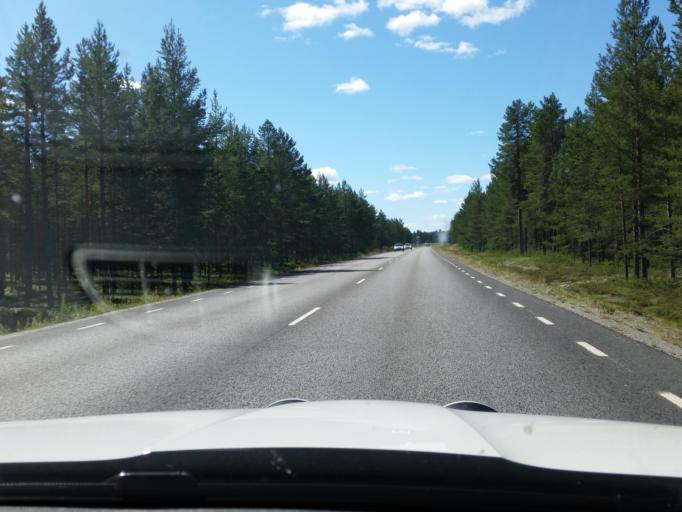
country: SE
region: Norrbotten
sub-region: Pitea Kommun
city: Pitea
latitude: 65.2432
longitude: 21.5311
